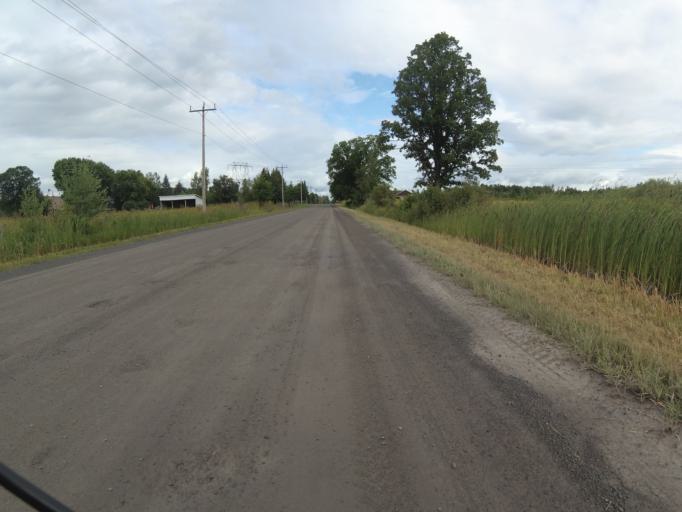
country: CA
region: Ontario
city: Clarence-Rockland
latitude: 45.4648
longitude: -75.3003
